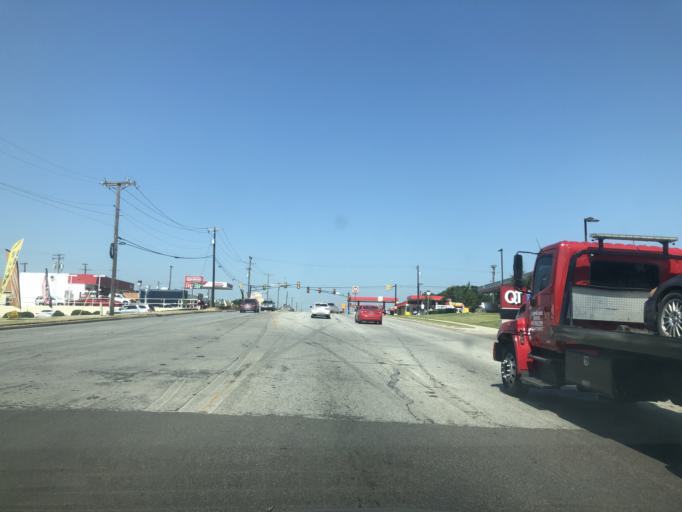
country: US
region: Texas
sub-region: Tarrant County
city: Haltom City
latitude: 32.7952
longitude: -97.3244
